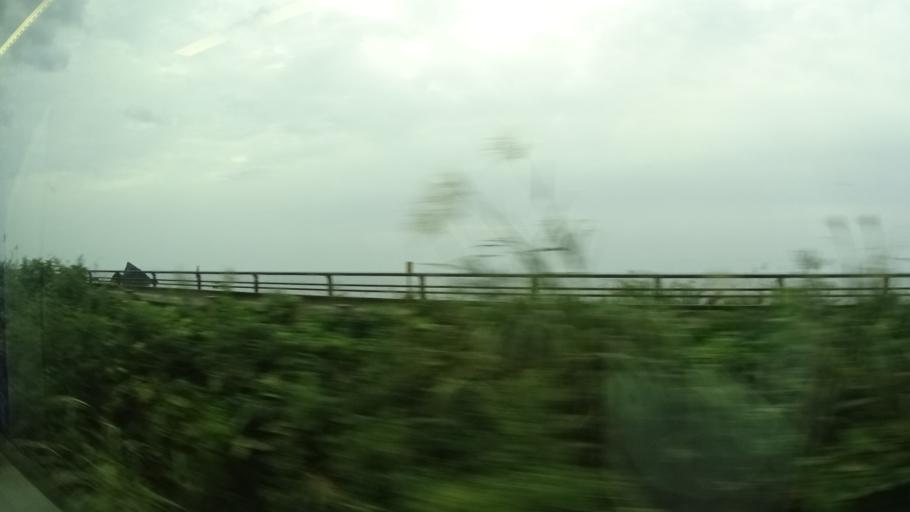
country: JP
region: Yamagata
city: Tsuruoka
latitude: 38.6152
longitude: 139.5794
